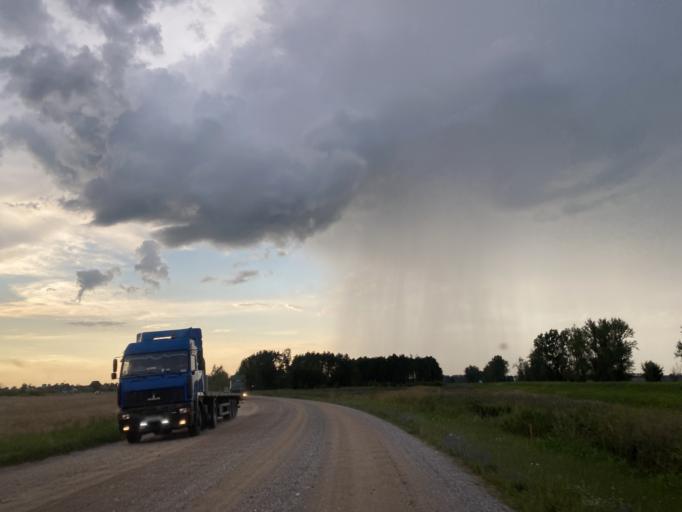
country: BY
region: Brest
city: Tsyelyakhany
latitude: 52.4943
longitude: 25.5709
